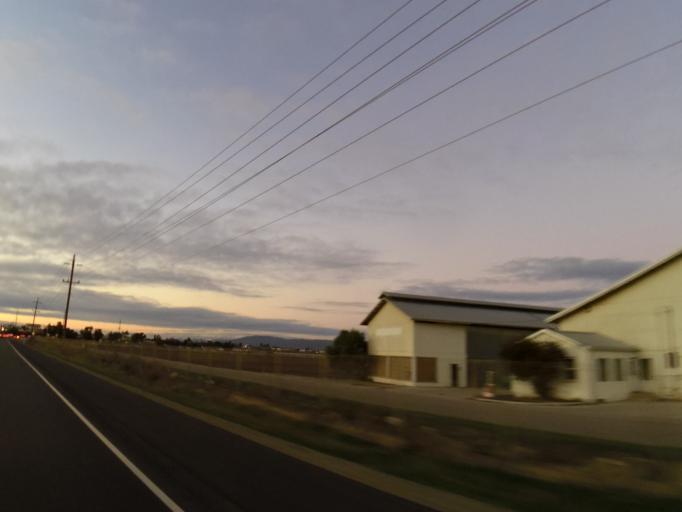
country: US
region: California
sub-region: Monterey County
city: Greenfield
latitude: 36.3089
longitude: -121.2293
